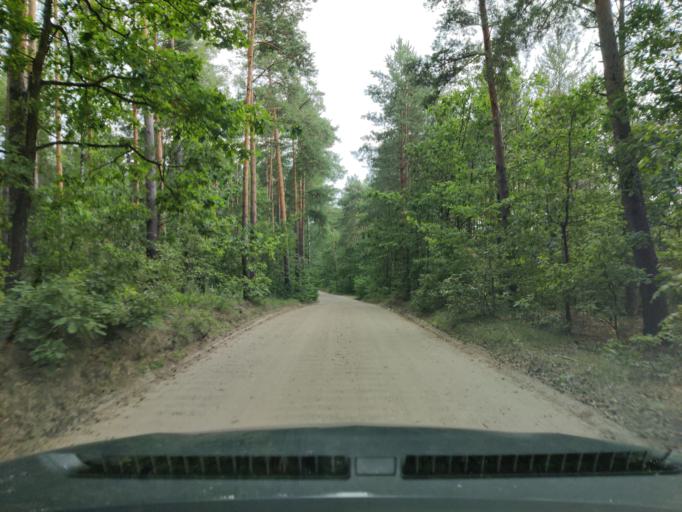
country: PL
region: Masovian Voivodeship
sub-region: Powiat pultuski
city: Pultusk
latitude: 52.7557
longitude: 21.1419
